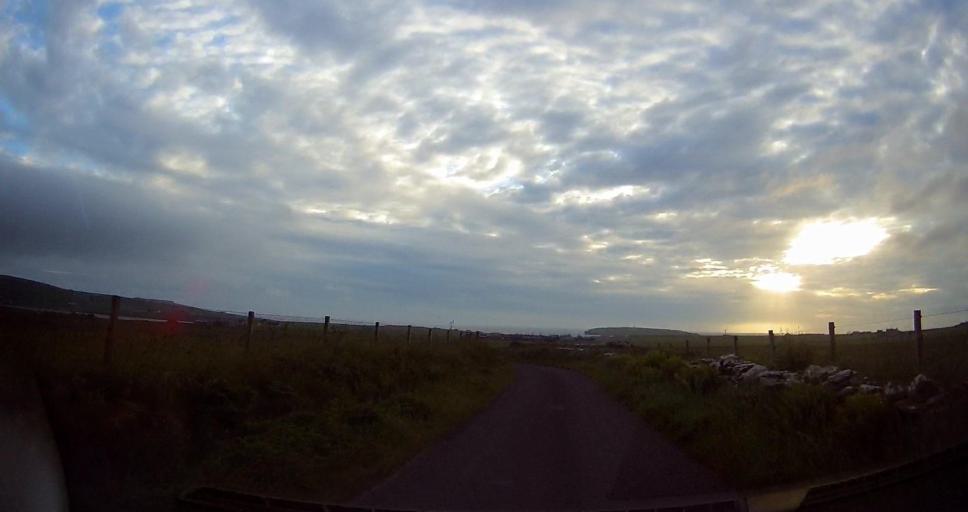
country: GB
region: Scotland
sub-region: Orkney Islands
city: Stromness
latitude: 59.1255
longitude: -3.2815
